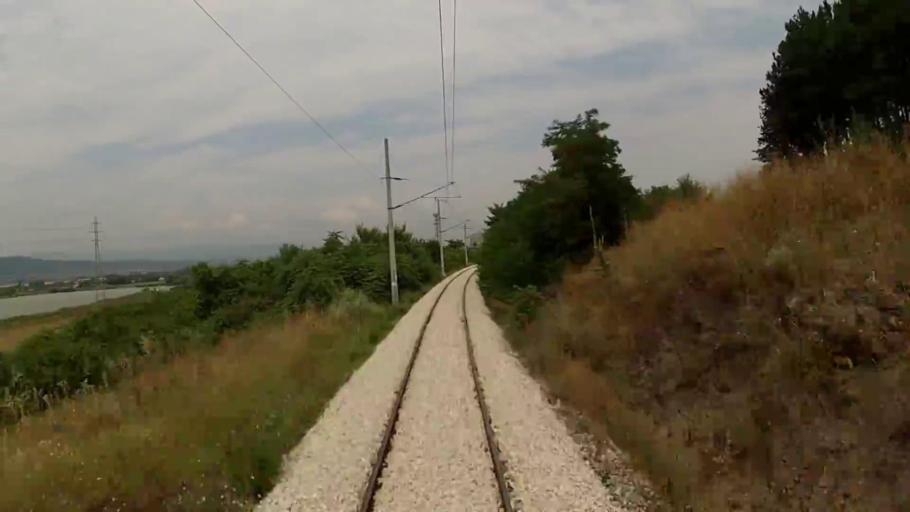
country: BG
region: Blagoevgrad
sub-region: Obshtina Blagoevgrad
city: Blagoevgrad
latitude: 41.9710
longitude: 23.0958
